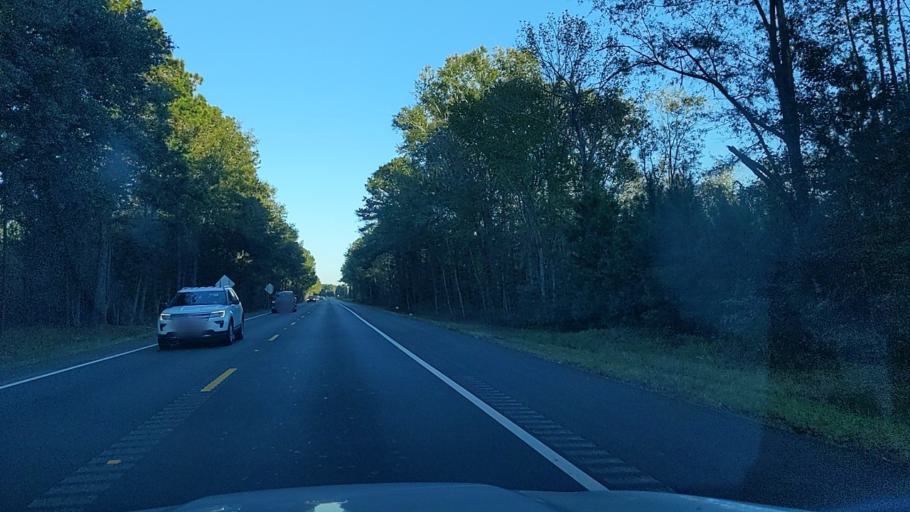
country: US
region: Georgia
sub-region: Chatham County
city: Port Wentworth
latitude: 32.1957
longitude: -81.2126
